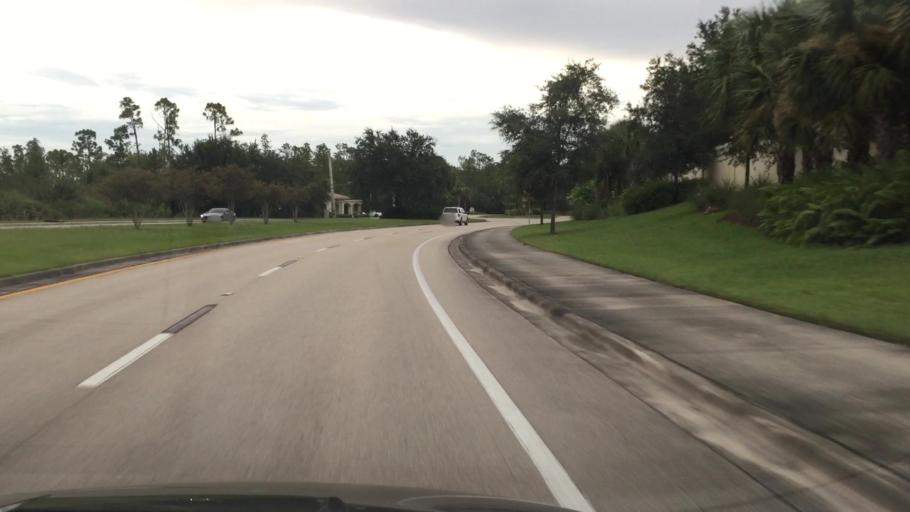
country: US
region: Florida
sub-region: Lee County
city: Gateway
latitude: 26.6013
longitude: -81.7859
